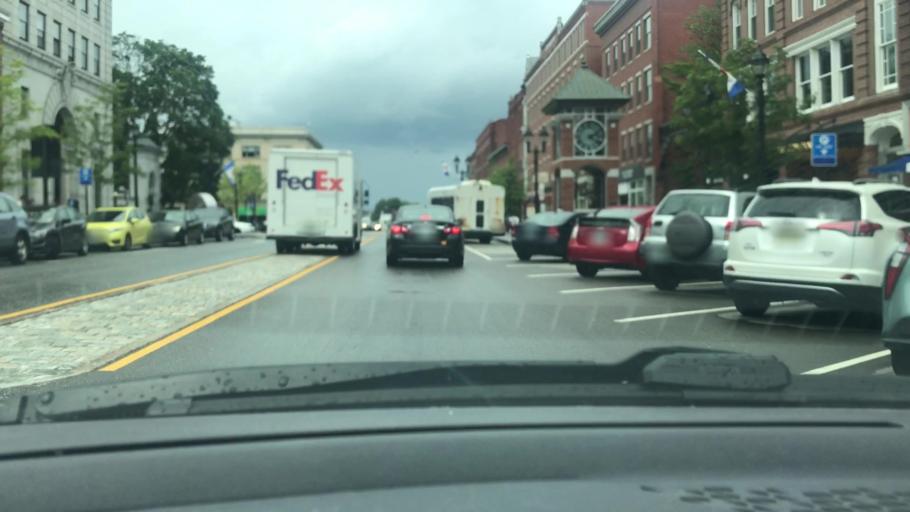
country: US
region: New Hampshire
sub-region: Merrimack County
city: Concord
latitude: 43.2063
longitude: -71.5363
